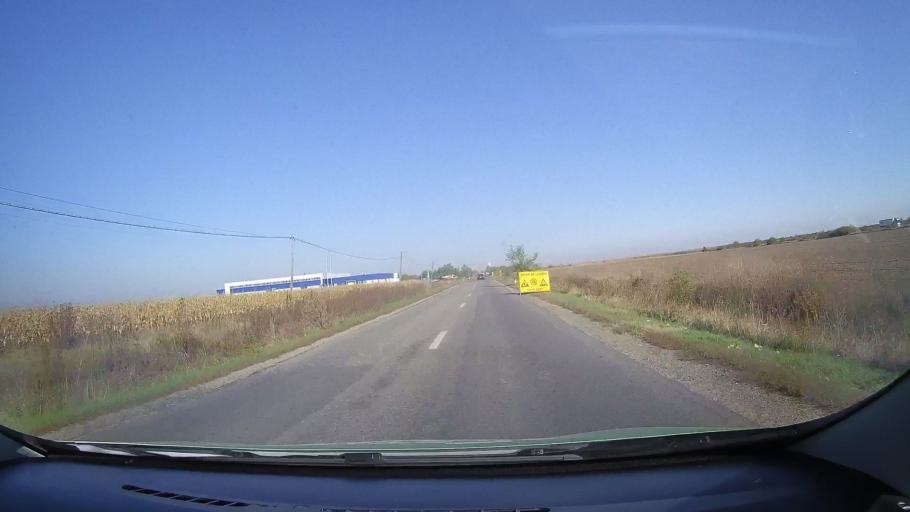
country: RO
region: Satu Mare
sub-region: Oras Tasnad
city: Tasnad
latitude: 47.5034
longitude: 22.5741
